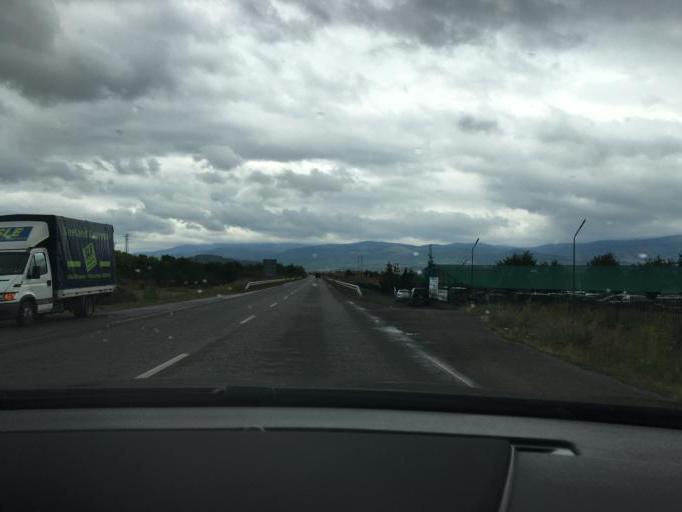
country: BG
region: Kyustendil
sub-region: Obshtina Kyustendil
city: Kyustendil
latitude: 42.2837
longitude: 22.7199
